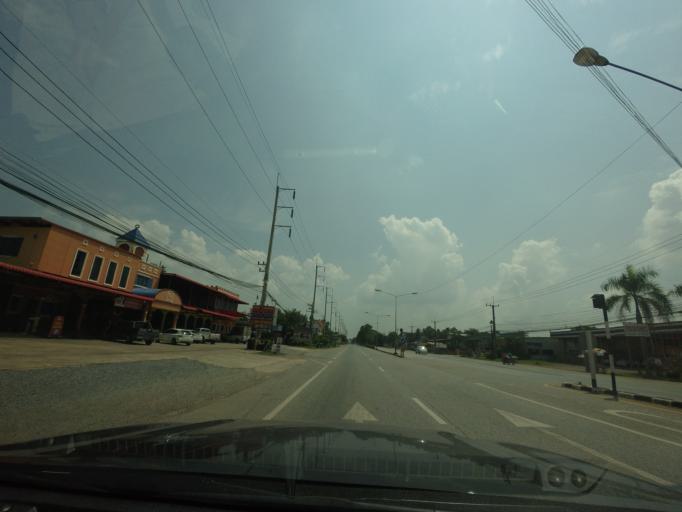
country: TH
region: Uttaradit
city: Uttaradit
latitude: 17.5921
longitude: 100.1322
